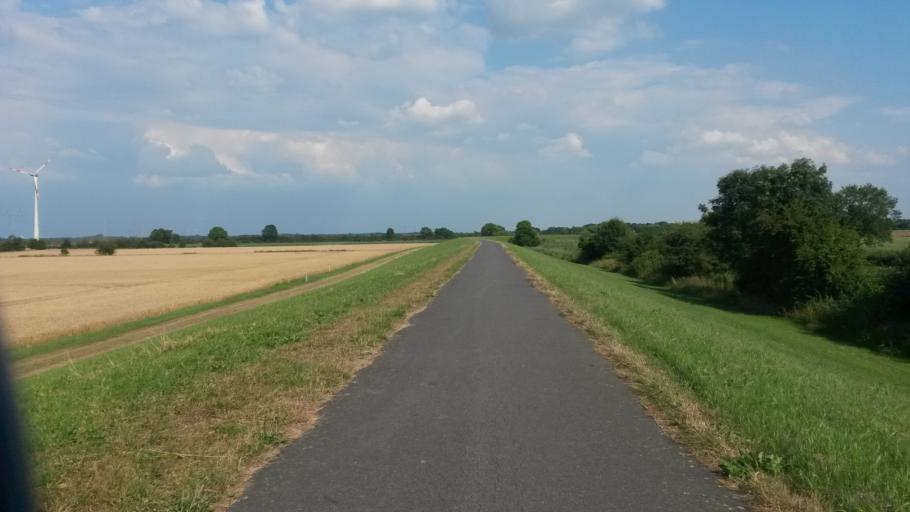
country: DE
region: Lower Saxony
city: Riede
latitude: 53.0175
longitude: 8.9157
